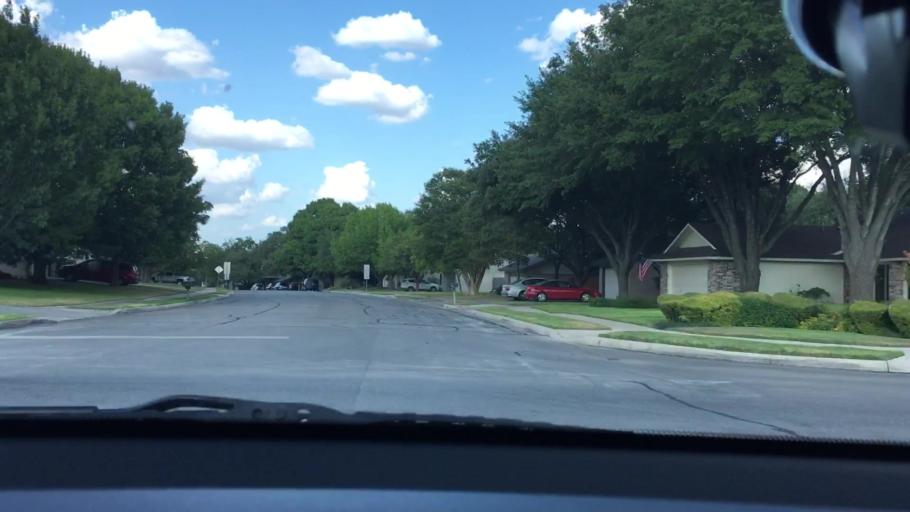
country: US
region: Texas
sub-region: Bexar County
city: Selma
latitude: 29.5685
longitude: -98.3167
